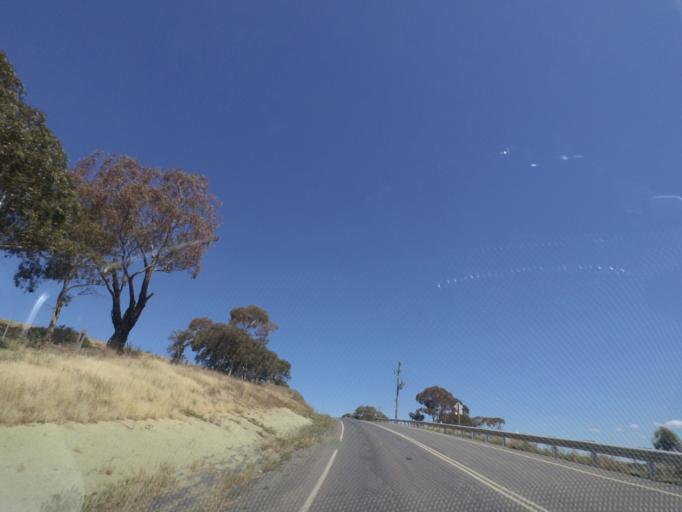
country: AU
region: Victoria
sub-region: Moorabool
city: Bacchus Marsh
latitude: -37.6986
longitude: 144.4564
